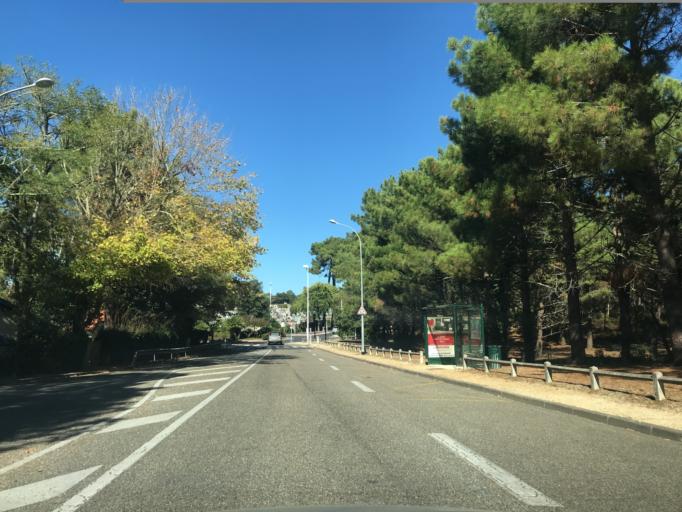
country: FR
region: Aquitaine
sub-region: Departement de la Gironde
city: Arcachon
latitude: 44.6521
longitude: -1.1808
